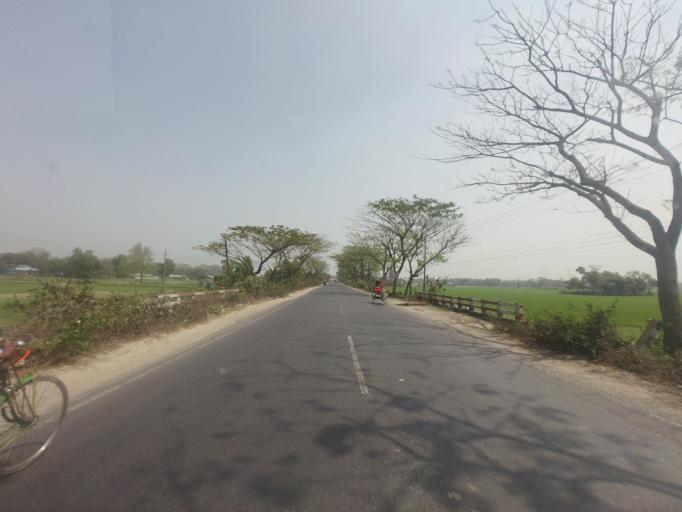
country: BD
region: Dhaka
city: Bhairab Bazar
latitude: 24.0496
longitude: 91.1075
